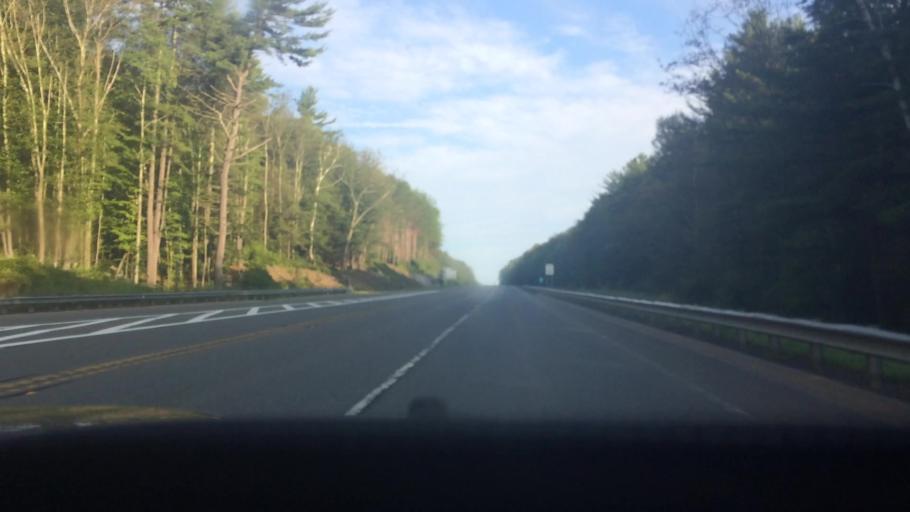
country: US
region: Massachusetts
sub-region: Franklin County
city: Orange
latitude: 42.5606
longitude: -72.3050
